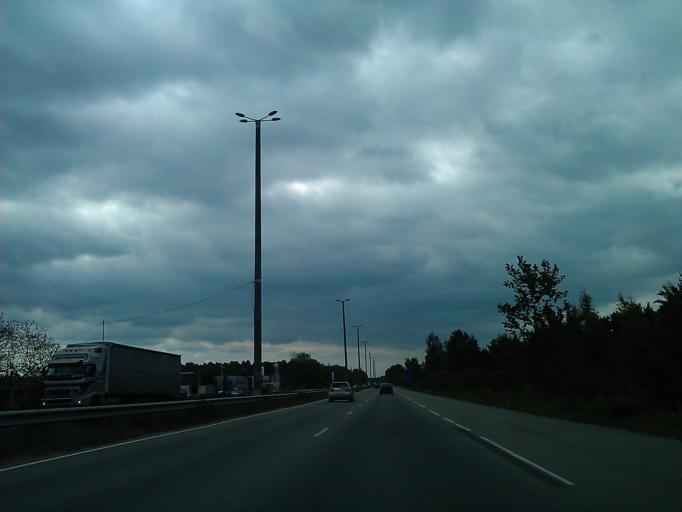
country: LV
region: Marupe
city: Marupe
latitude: 56.8849
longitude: 24.0737
